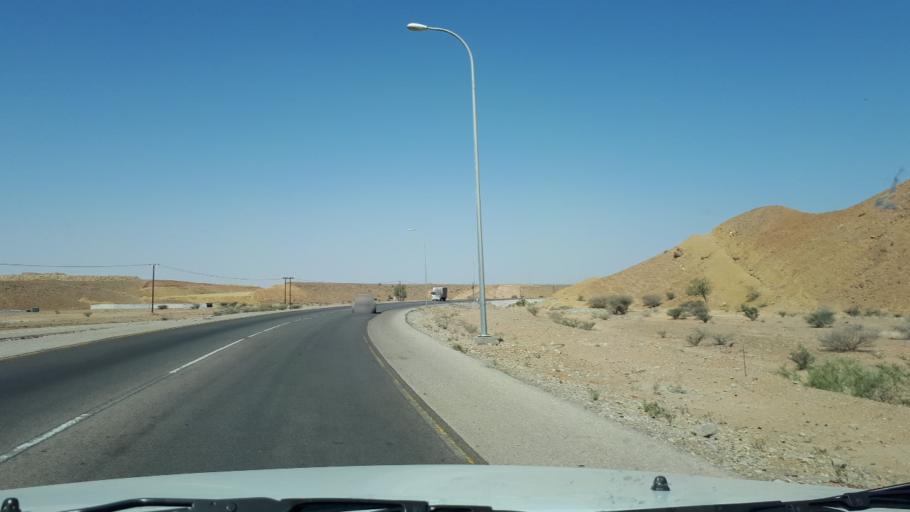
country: OM
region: Ash Sharqiyah
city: Sur
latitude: 22.3157
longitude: 59.3052
